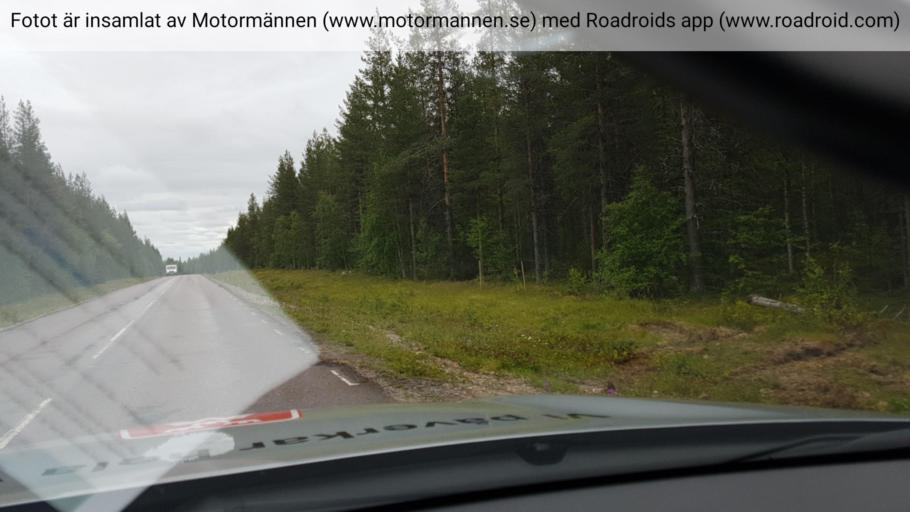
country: SE
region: Norrbotten
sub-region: Overkalix Kommun
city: OEverkalix
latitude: 67.0598
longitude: 22.2914
